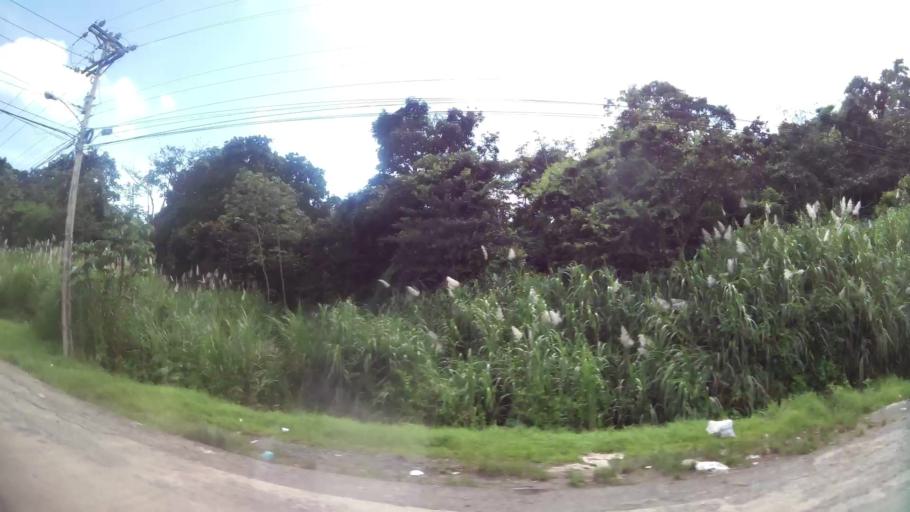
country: PA
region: Panama
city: Las Cumbres
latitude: 9.0395
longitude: -79.5463
